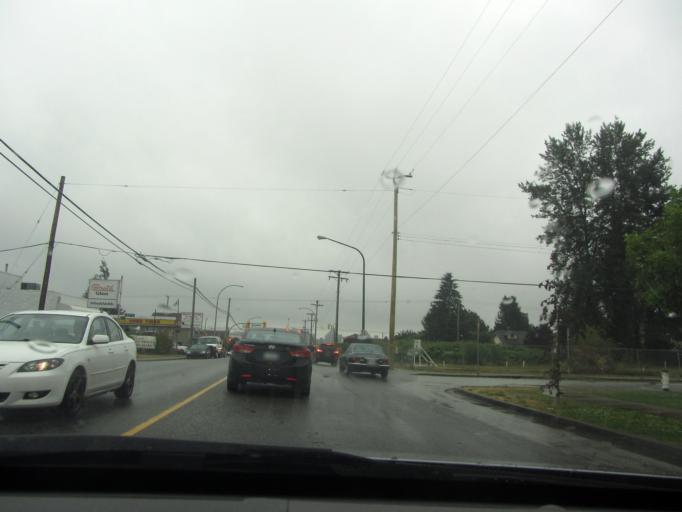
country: CA
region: British Columbia
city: New Westminster
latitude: 49.2246
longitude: -122.9348
